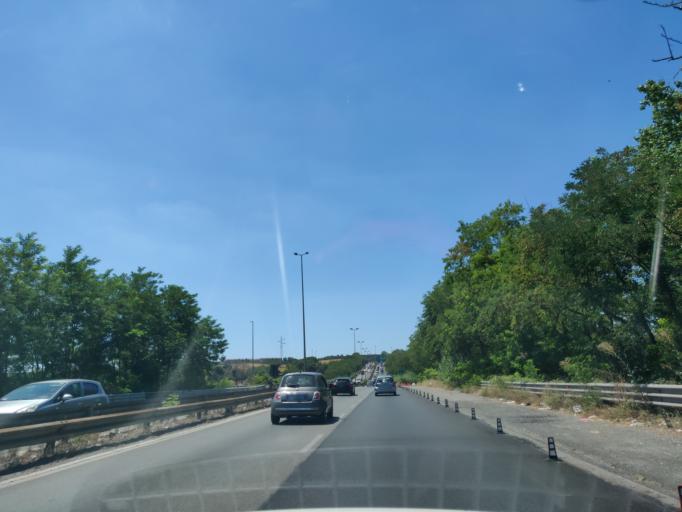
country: IT
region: Latium
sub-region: Citta metropolitana di Roma Capitale
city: Selcetta
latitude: 41.8104
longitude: 12.4583
